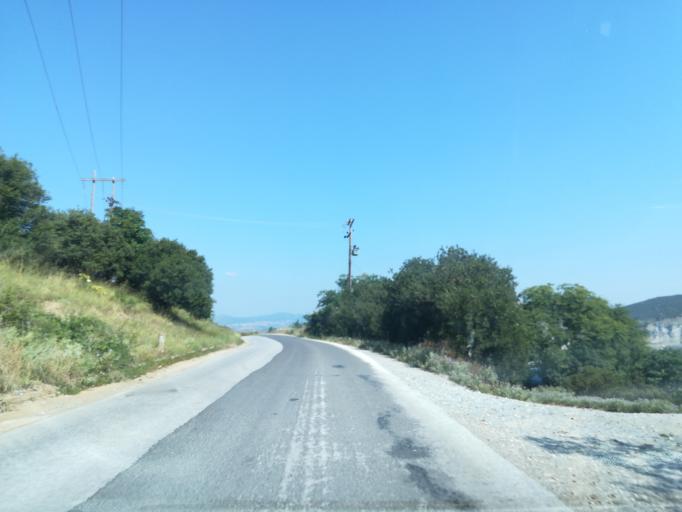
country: GR
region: Central Macedonia
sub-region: Nomos Thessalonikis
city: Asvestochori
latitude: 40.6356
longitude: 23.0204
